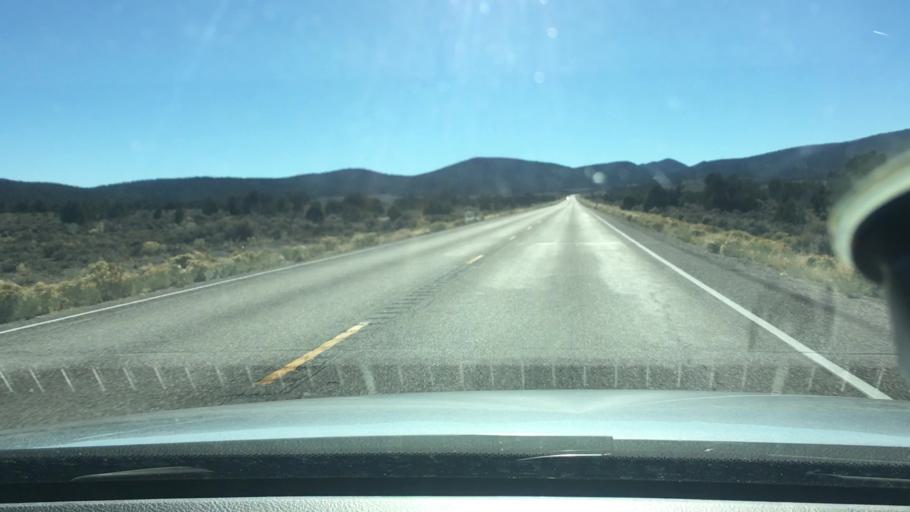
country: US
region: Nevada
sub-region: White Pine County
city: Ely
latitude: 38.8479
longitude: -115.2447
